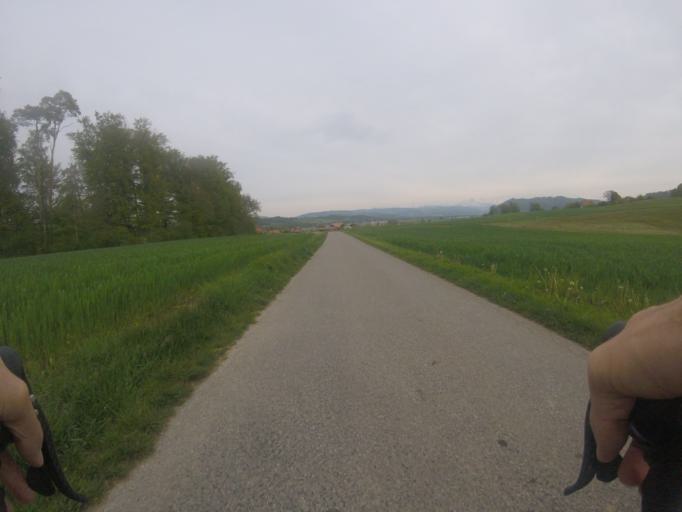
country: CH
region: Bern
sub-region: Bern-Mittelland District
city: Muri
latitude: 46.9172
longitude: 7.4870
